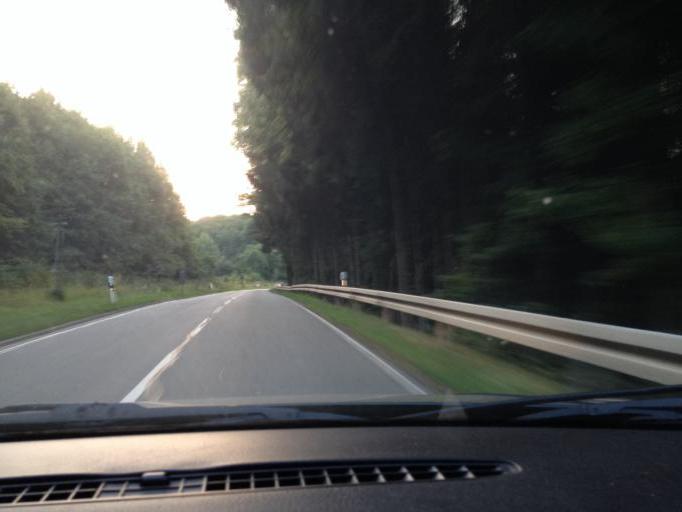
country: DE
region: Rheinland-Pfalz
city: Achtelsbach
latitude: 49.5860
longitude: 7.0701
